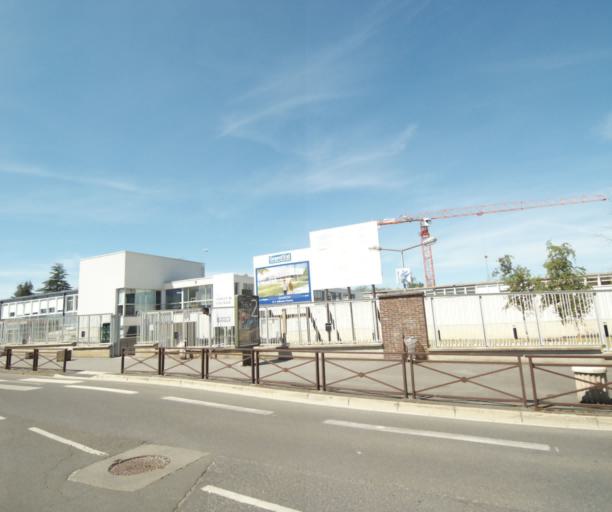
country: FR
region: Champagne-Ardenne
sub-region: Departement des Ardennes
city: Charleville-Mezieres
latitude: 49.7488
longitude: 4.7143
